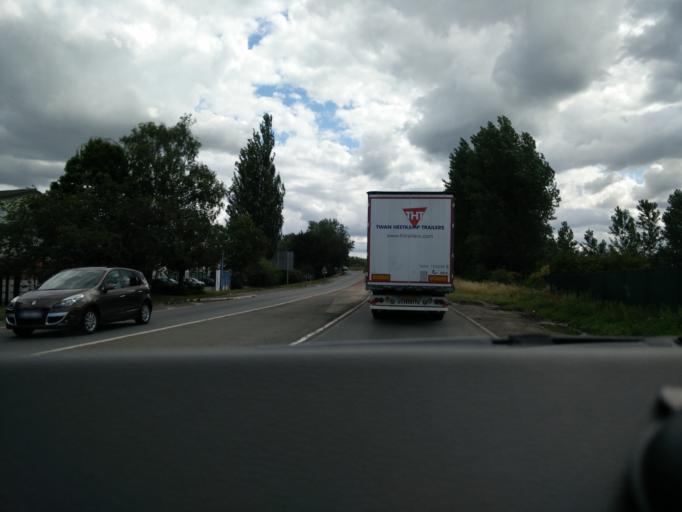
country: FR
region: Nord-Pas-de-Calais
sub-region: Departement du Nord
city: Bergues
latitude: 50.9518
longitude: 2.4311
